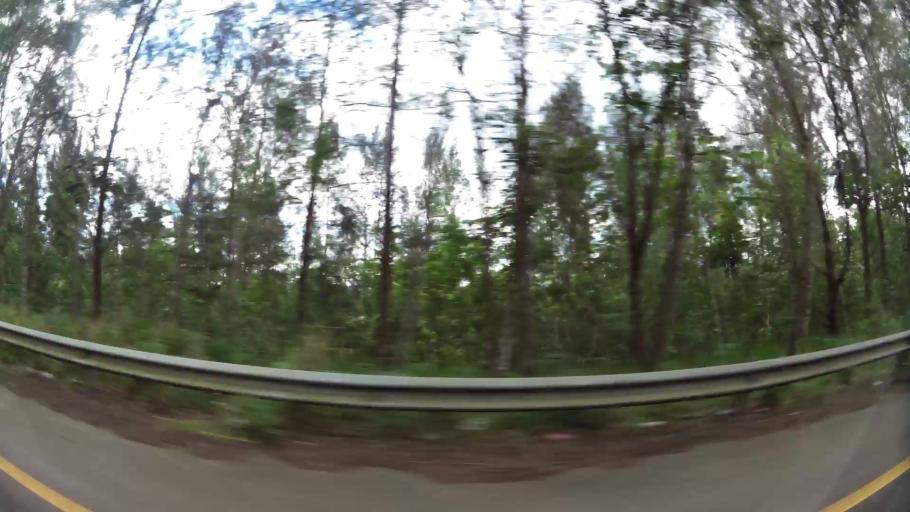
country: DO
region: Monsenor Nouel
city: Sabana del Puerto
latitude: 19.0844
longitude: -70.4421
